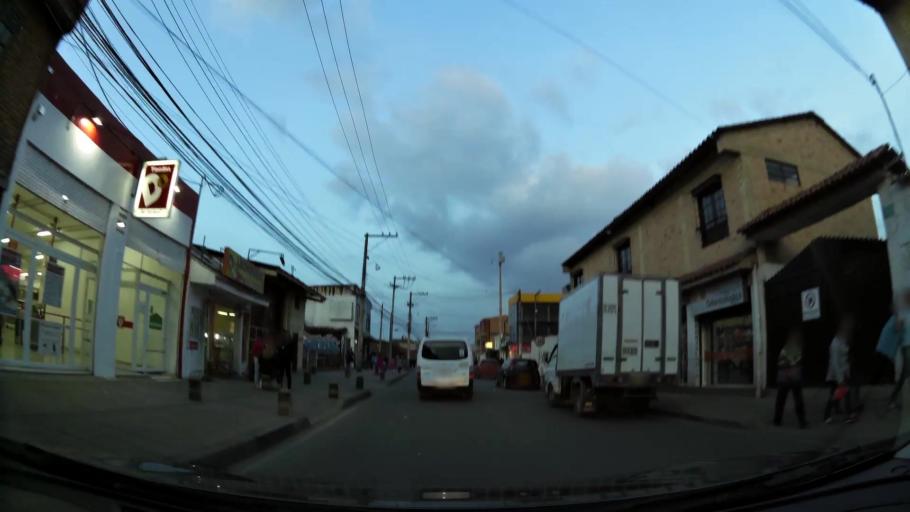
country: CO
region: Cundinamarca
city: Funza
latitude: 4.7161
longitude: -74.2096
